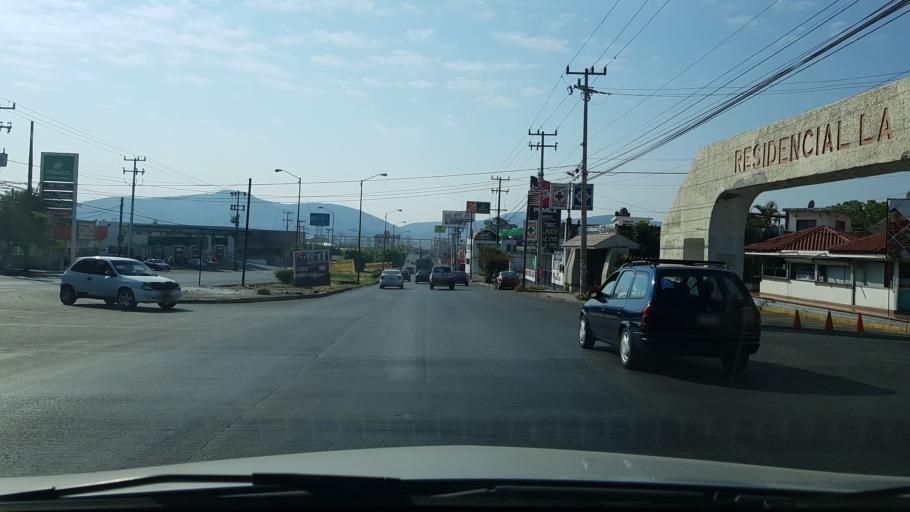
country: MX
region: Morelos
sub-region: Jiutepec
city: Jiutepec
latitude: 18.9009
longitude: -99.1728
